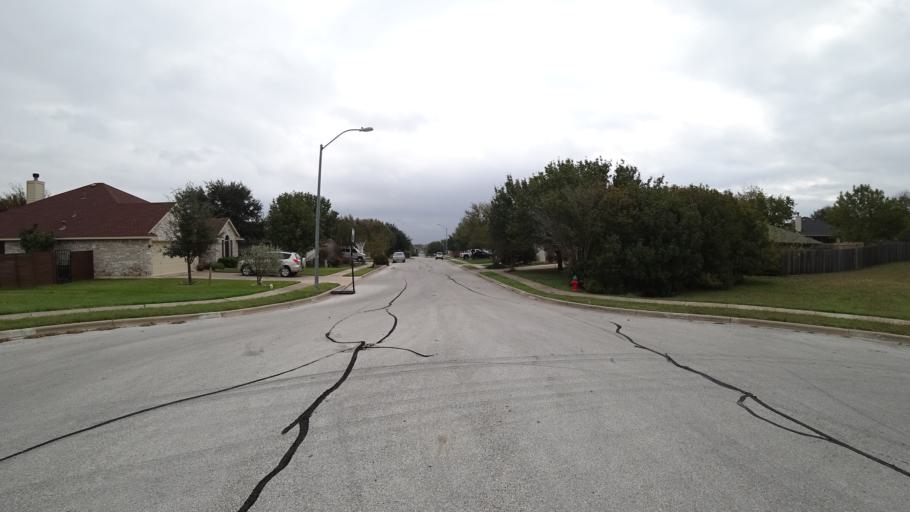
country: US
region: Texas
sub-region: Travis County
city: Pflugerville
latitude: 30.4432
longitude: -97.6053
